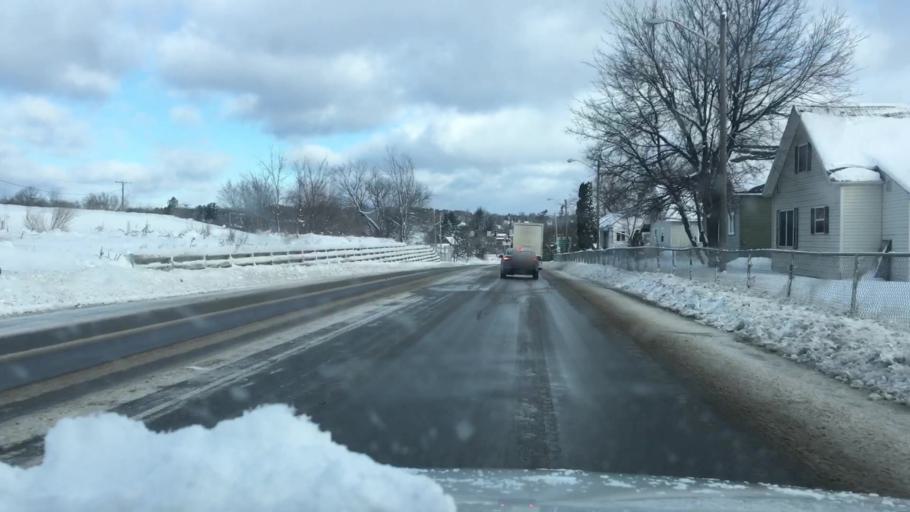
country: US
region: Maine
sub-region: Aroostook County
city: Caribou
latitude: 46.8521
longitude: -68.0054
